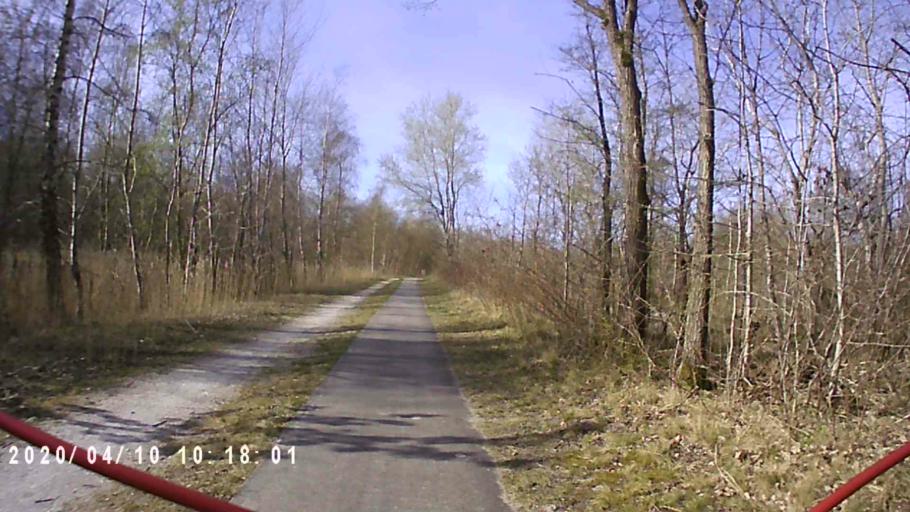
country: NL
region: Friesland
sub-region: Gemeente Dongeradeel
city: Anjum
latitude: 53.3824
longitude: 6.2312
